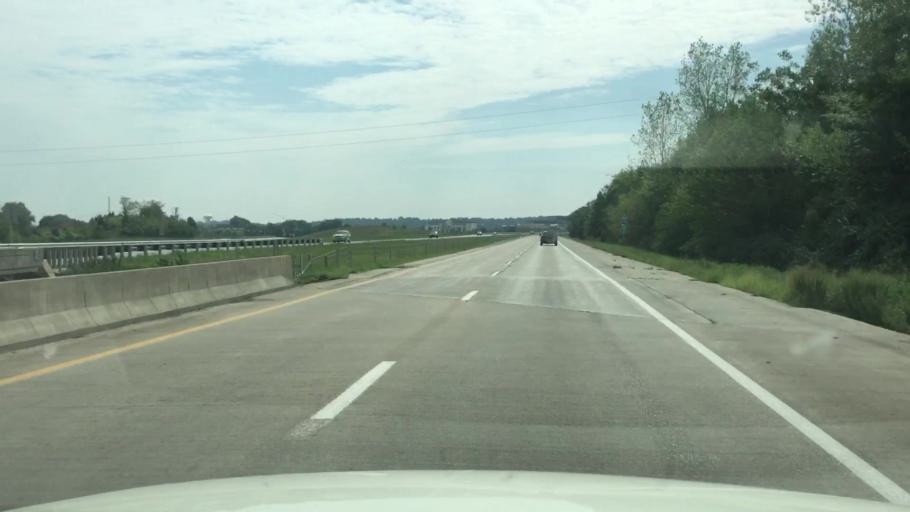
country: US
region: Missouri
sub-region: Clay County
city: Liberty
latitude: 39.2862
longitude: -94.4164
